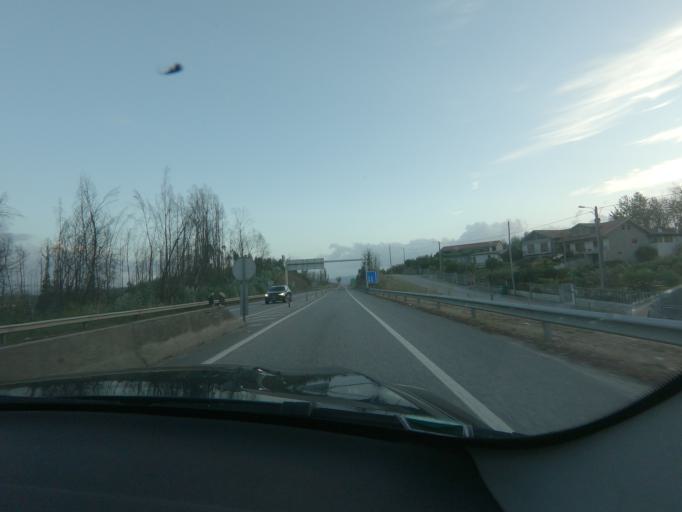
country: PT
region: Viseu
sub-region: Mortagua
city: Mortagua
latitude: 40.3504
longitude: -8.2049
